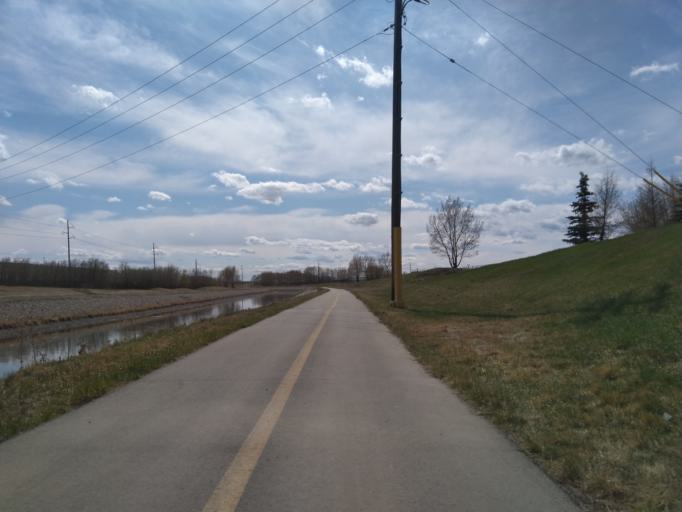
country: CA
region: Alberta
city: Chestermere
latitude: 50.9678
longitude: -113.9466
